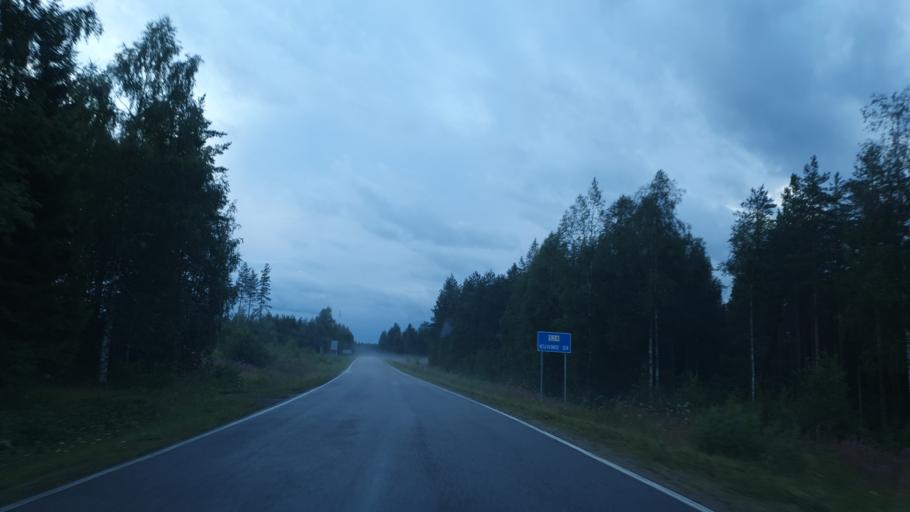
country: FI
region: Kainuu
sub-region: Kehys-Kainuu
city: Kuhmo
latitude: 63.9543
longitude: 29.7183
